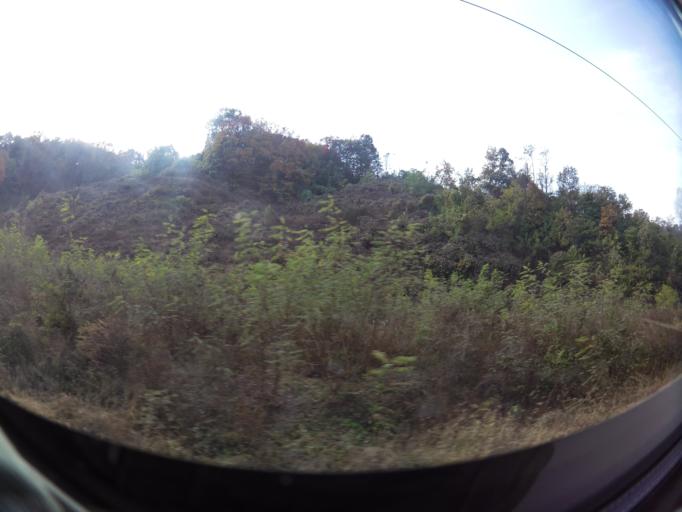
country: KR
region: Gyeongsangbuk-do
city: Gimcheon
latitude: 36.1347
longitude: 128.0182
